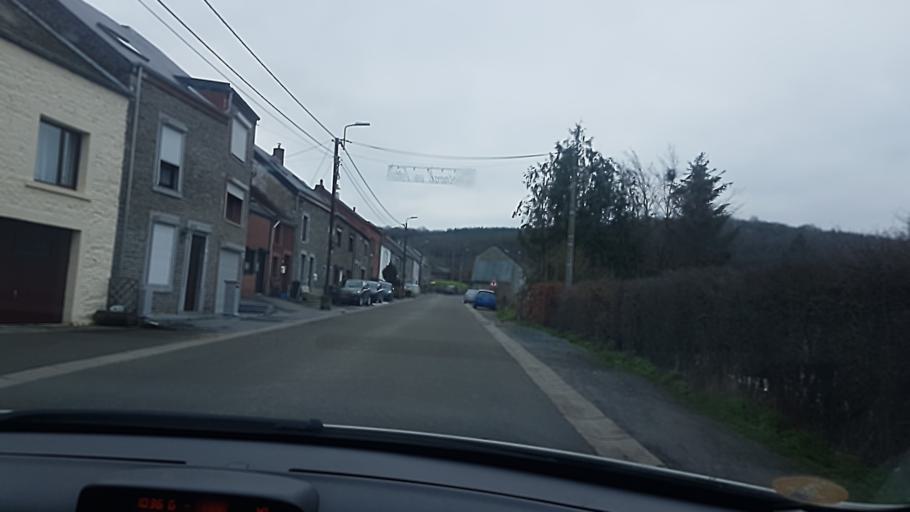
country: BE
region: Wallonia
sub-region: Province de Namur
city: Couvin
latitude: 50.0673
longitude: 4.6070
